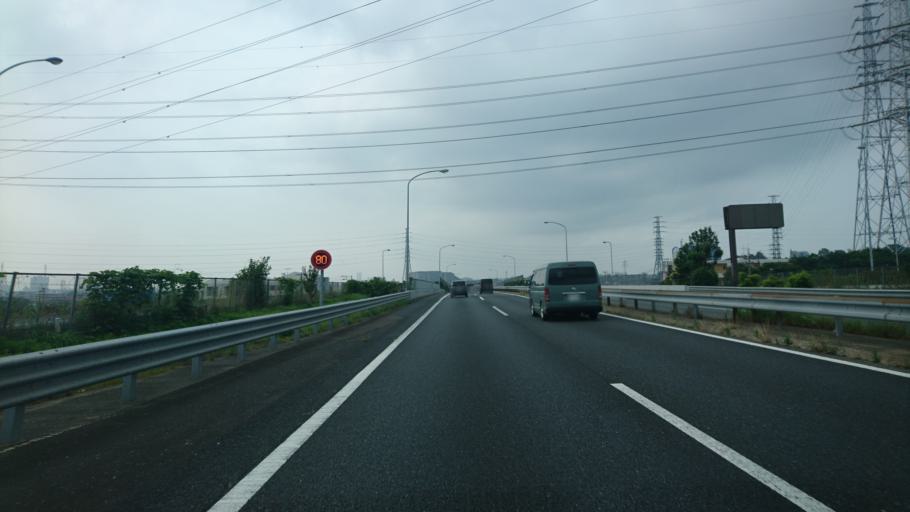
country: JP
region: Chiba
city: Chiba
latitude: 35.5638
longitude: 140.1382
